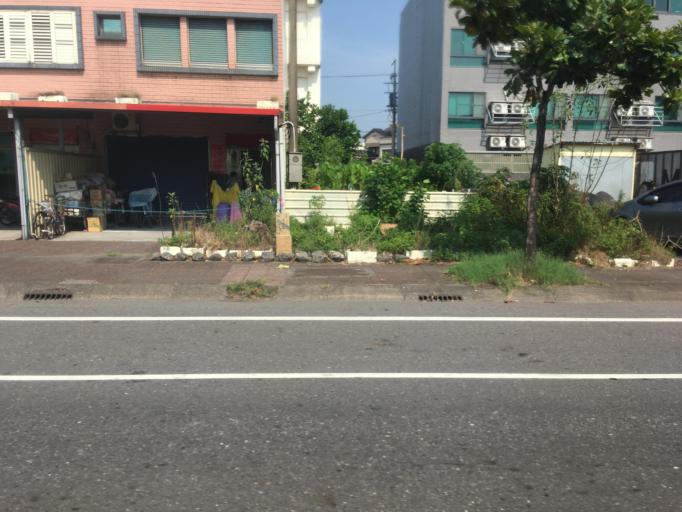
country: TW
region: Taiwan
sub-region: Yilan
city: Yilan
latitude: 24.6424
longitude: 121.8348
